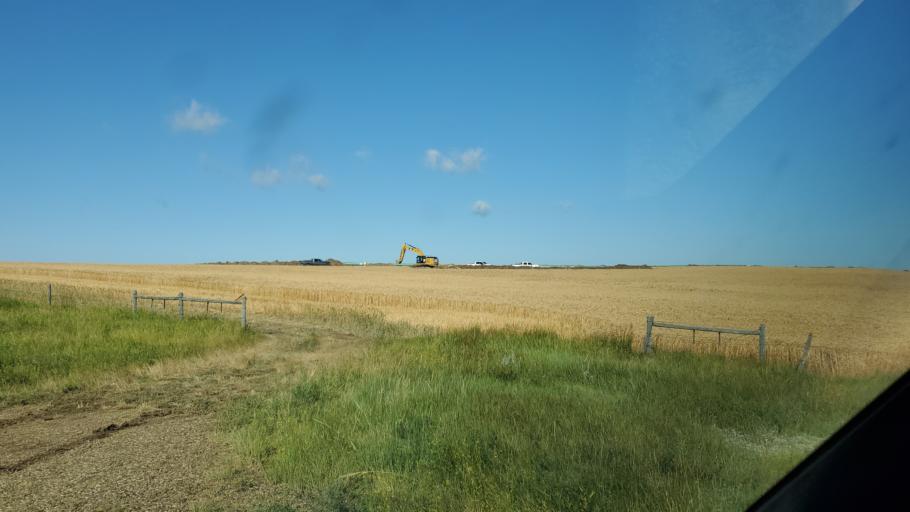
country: US
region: Montana
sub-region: Fallon County
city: Baker
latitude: 46.2834
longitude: -104.3111
